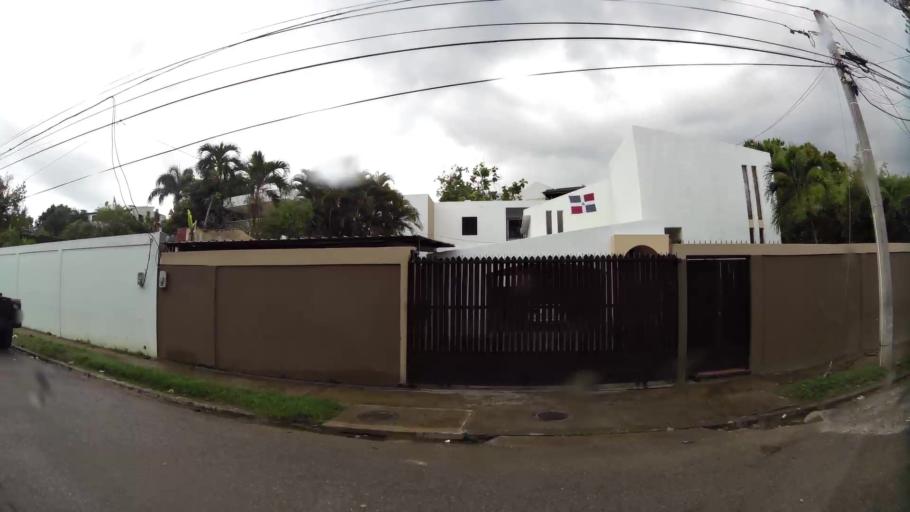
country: DO
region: Nacional
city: La Agustina
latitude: 18.5009
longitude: -69.9395
